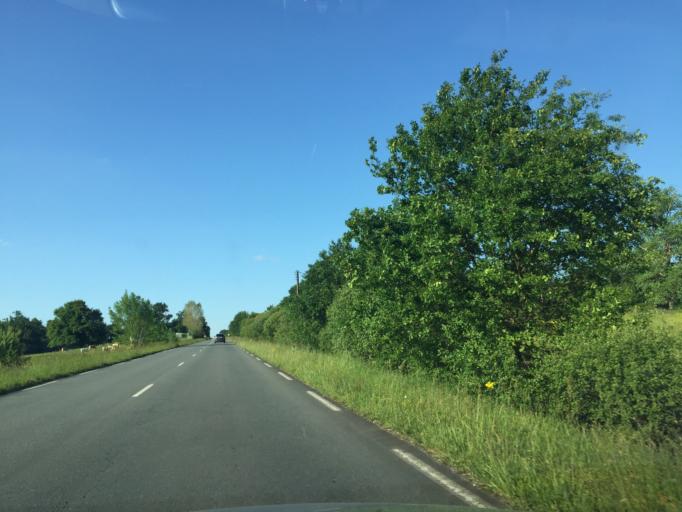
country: FR
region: Aquitaine
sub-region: Departement de la Dordogne
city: La Roche-Chalais
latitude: 45.1815
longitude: 0.0248
